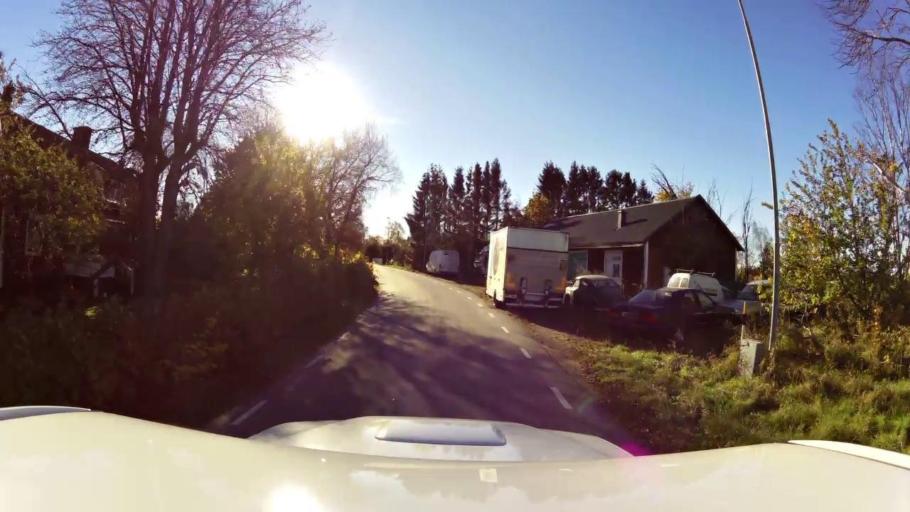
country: SE
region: OEstergoetland
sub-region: Linkopings Kommun
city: Ljungsbro
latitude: 58.4932
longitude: 15.4193
